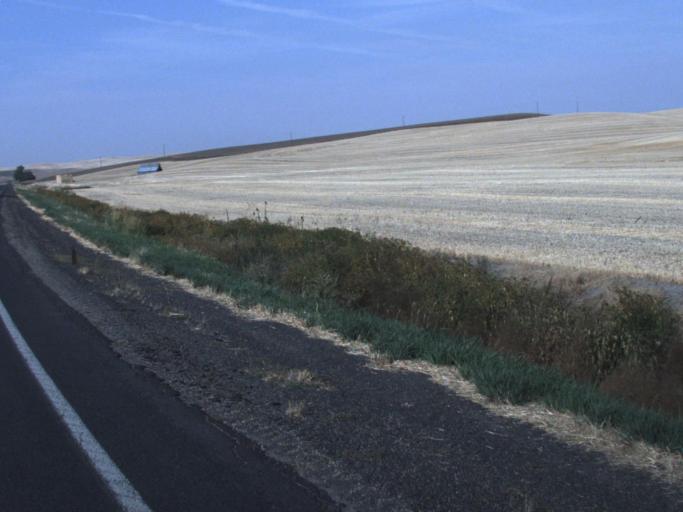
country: US
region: Idaho
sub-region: Benewah County
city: Plummer
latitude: 47.1852
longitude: -117.1615
